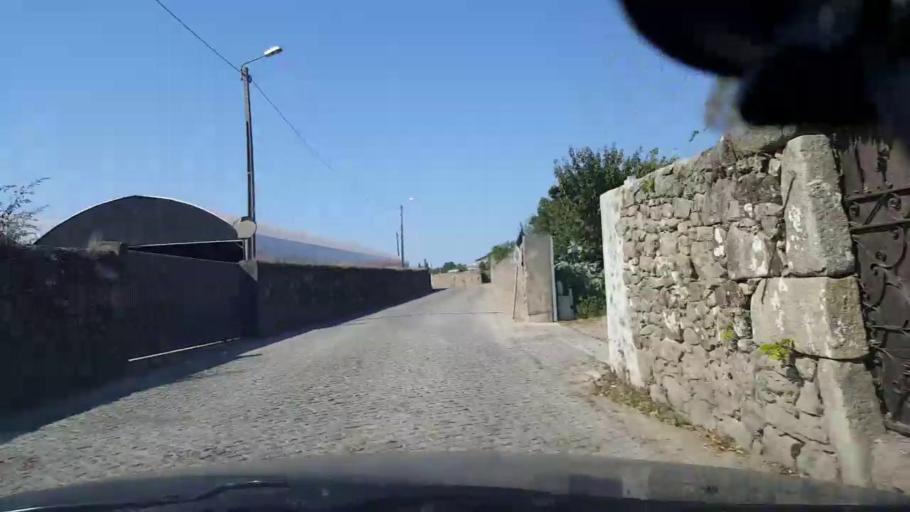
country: PT
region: Porto
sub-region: Povoa de Varzim
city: Pedroso
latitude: 41.4011
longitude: -8.6906
